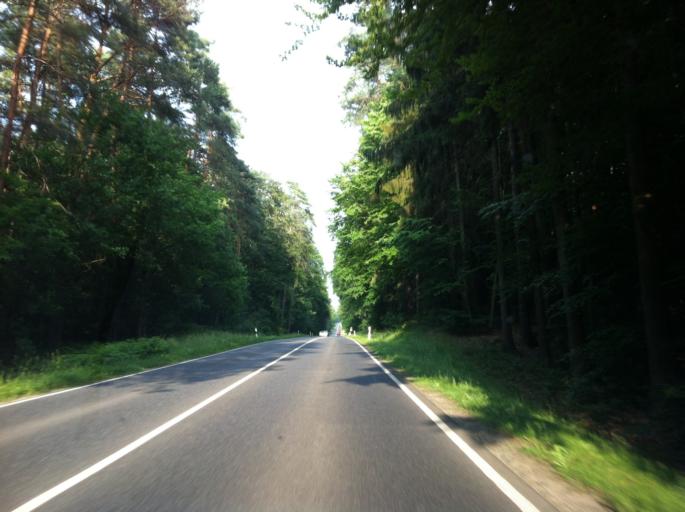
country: DE
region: Hesse
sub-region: Regierungsbezirk Darmstadt
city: Schaafheim
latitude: 49.9588
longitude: 9.0217
